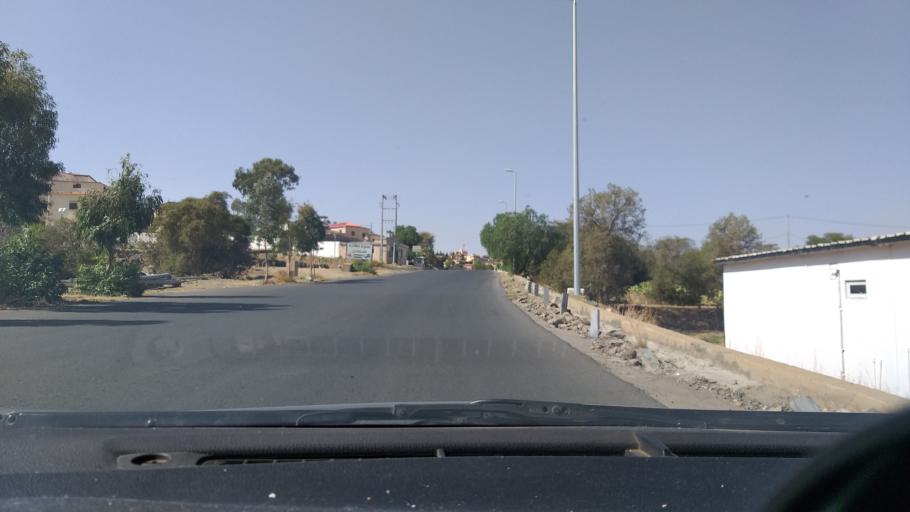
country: SA
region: Makkah
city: Ash Shafa
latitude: 21.0702
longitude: 40.3244
